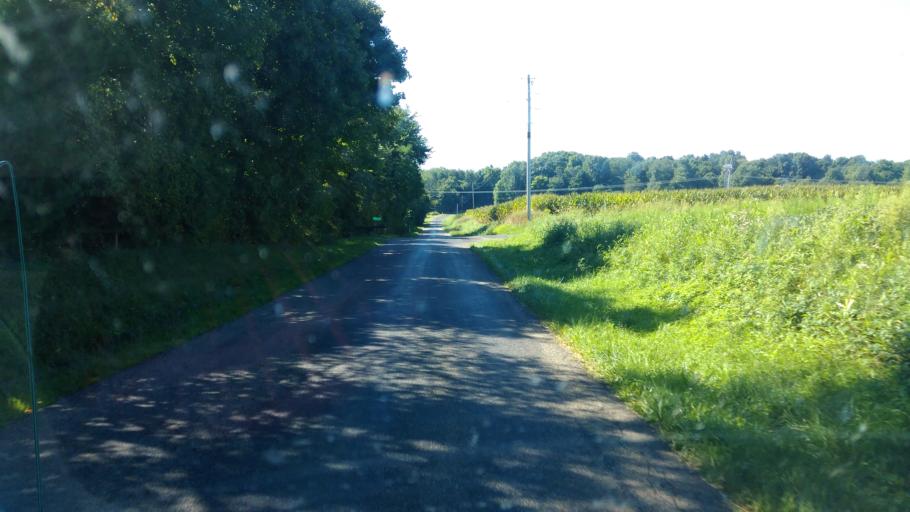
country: US
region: Ohio
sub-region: Knox County
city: Mount Vernon
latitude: 40.4562
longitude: -82.4680
